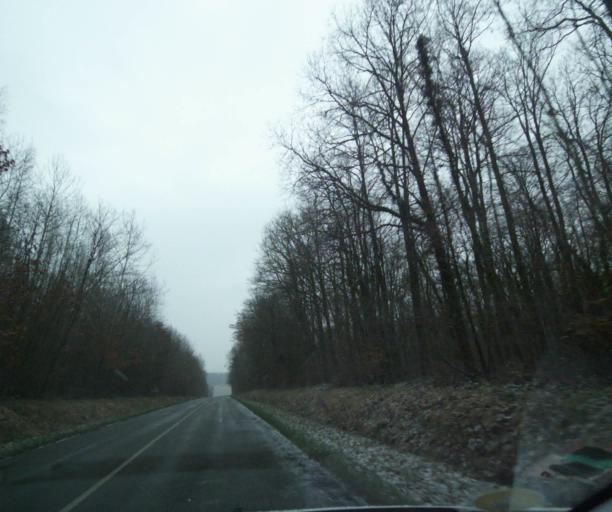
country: FR
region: Champagne-Ardenne
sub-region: Departement de la Haute-Marne
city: Wassy
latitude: 48.4728
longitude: 5.0200
